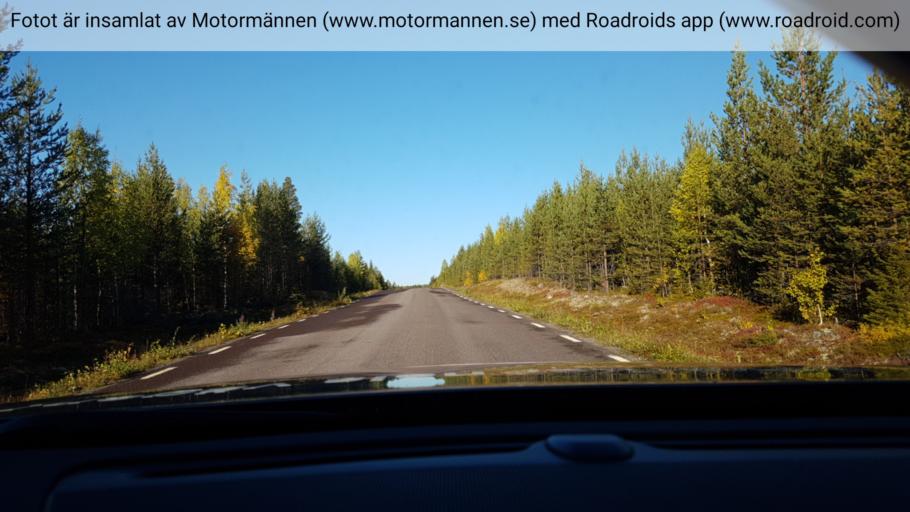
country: SE
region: Norrbotten
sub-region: Bodens Kommun
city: Boden
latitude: 66.0067
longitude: 21.5692
